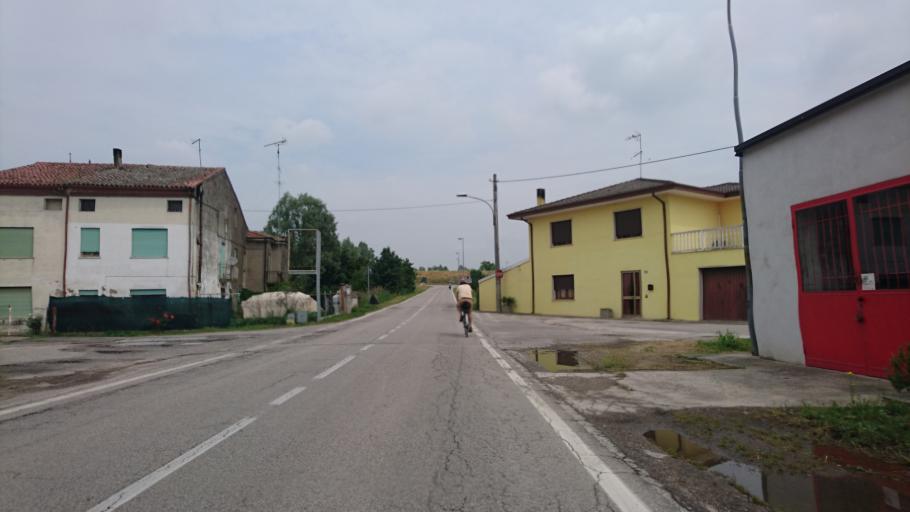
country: IT
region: Veneto
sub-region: Provincia di Rovigo
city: Lendinara
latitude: 45.1064
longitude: 11.6149
